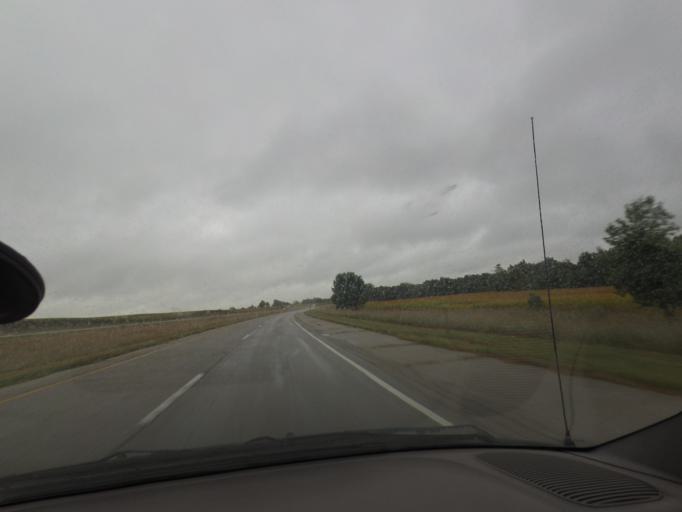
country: US
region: Illinois
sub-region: Pike County
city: Barry
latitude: 39.7399
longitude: -91.1343
